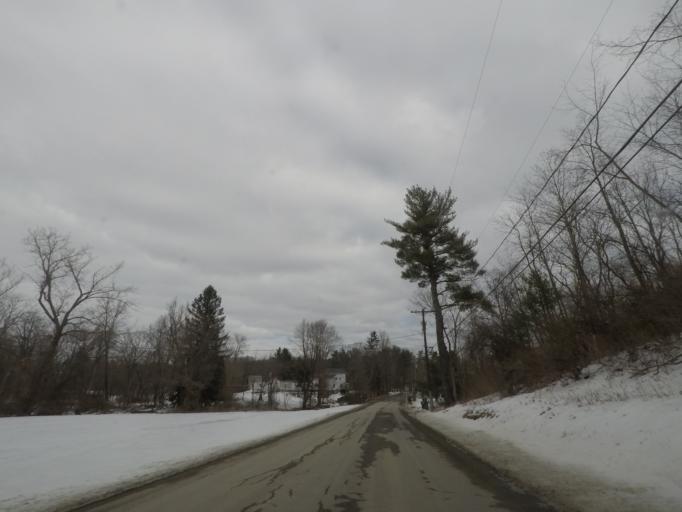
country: US
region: New York
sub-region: Rensselaer County
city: Poestenkill
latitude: 42.7362
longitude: -73.5710
